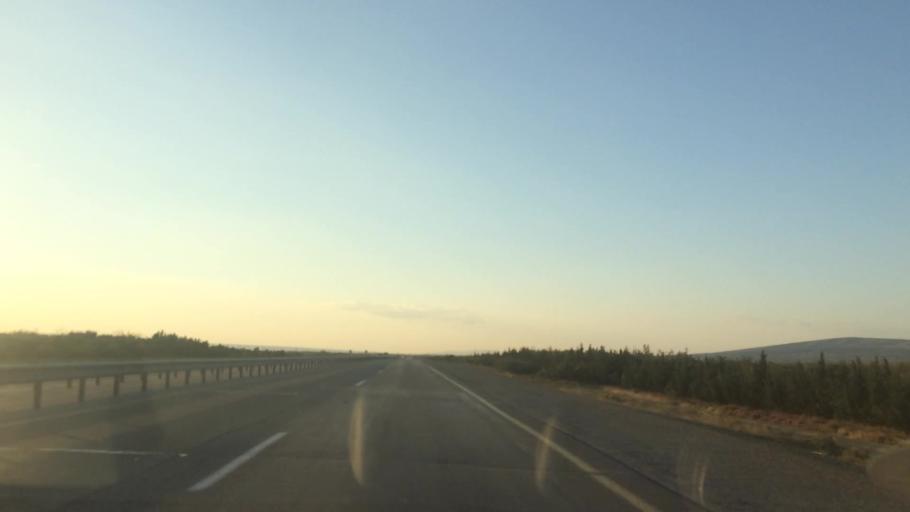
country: AZ
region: Baki
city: Qobustan
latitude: 39.9509
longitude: 49.3228
